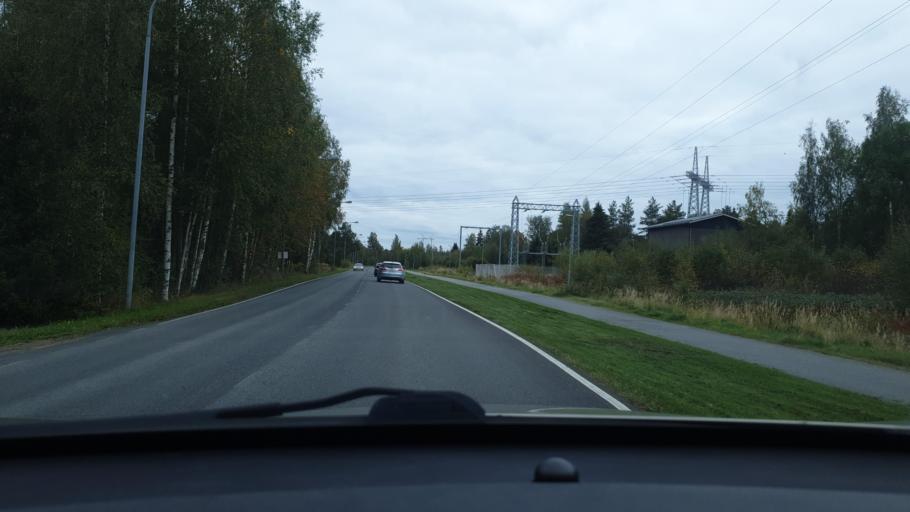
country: FI
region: Ostrobothnia
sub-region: Vaasa
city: Teeriniemi
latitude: 63.0937
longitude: 21.6976
